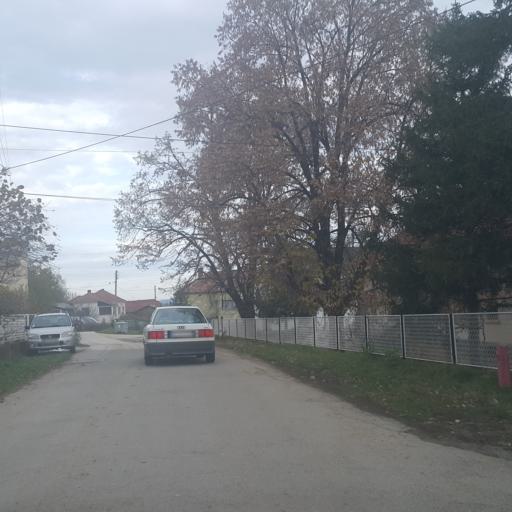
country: RS
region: Central Serbia
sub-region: Zajecarski Okrug
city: Knjazevac
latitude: 43.5978
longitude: 22.2564
